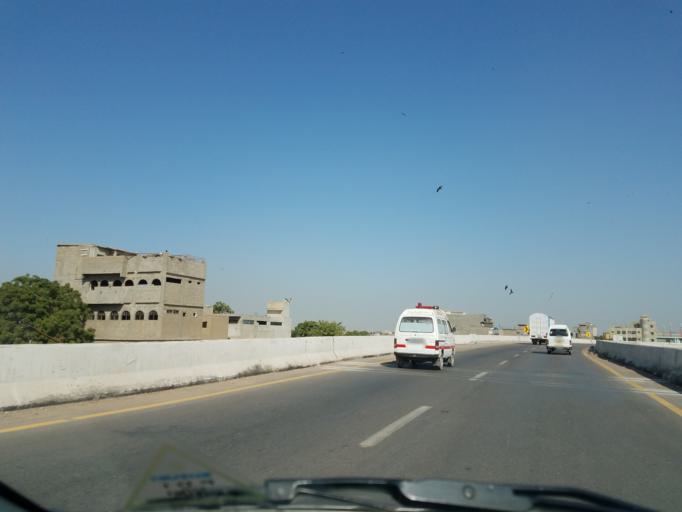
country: PK
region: Sindh
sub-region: Karachi District
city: Karachi
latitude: 24.8821
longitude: 67.0034
